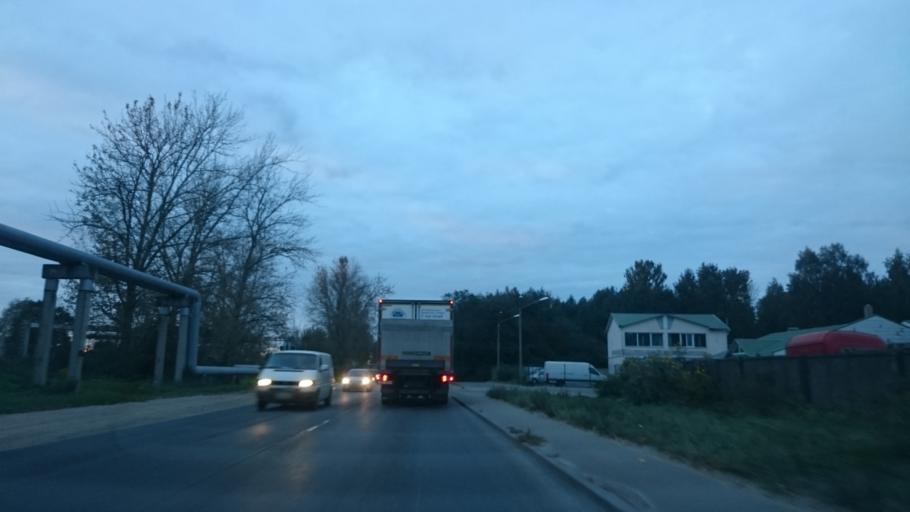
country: LV
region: Kekava
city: Balozi
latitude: 56.9142
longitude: 24.2016
